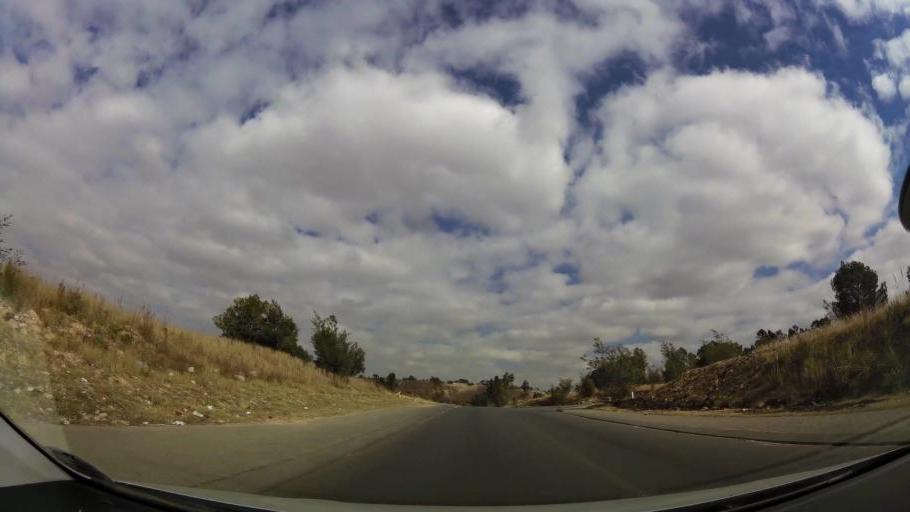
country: ZA
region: Gauteng
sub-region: City of Johannesburg Metropolitan Municipality
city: Roodepoort
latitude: -26.1935
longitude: 27.9023
